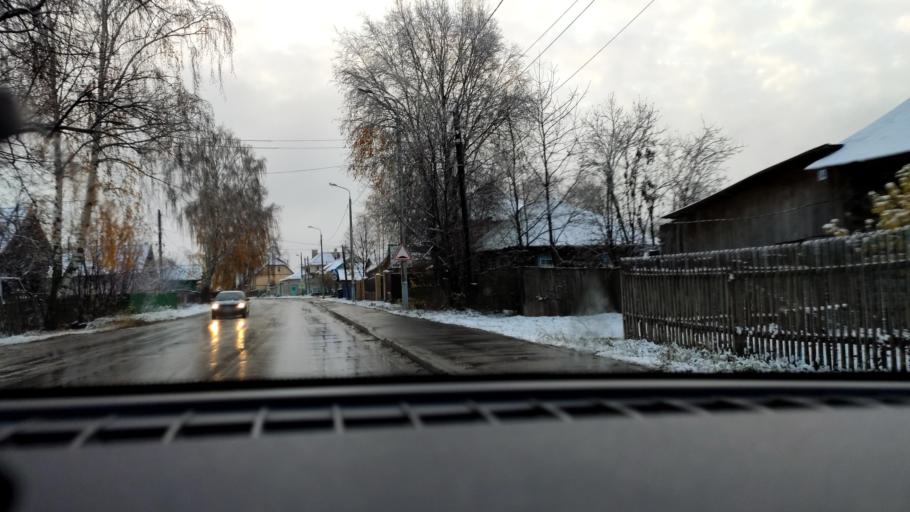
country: RU
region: Perm
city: Kondratovo
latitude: 58.0465
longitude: 56.0443
